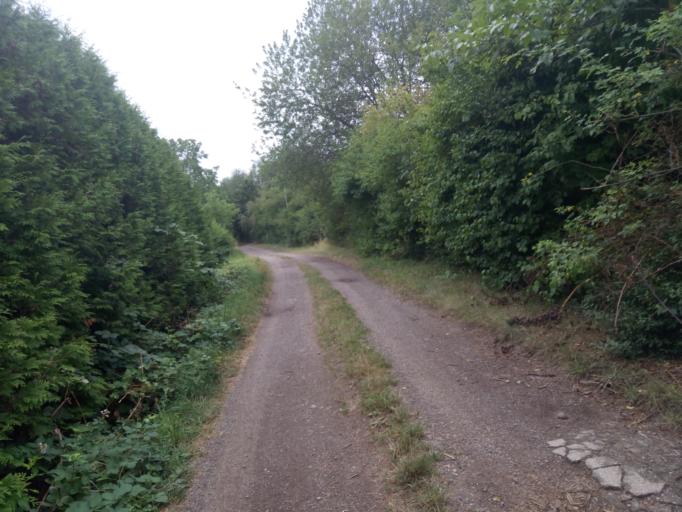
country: DE
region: Rheinland-Pfalz
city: Waldlaubersheim
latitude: 49.9251
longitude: 7.8311
